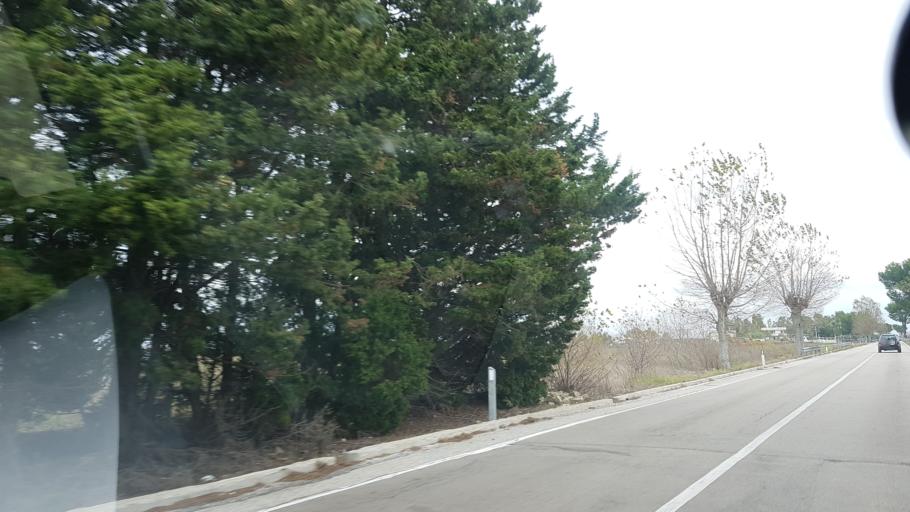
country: IT
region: Apulia
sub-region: Provincia di Brindisi
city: San Pancrazio Salentino
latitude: 40.4132
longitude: 17.8600
